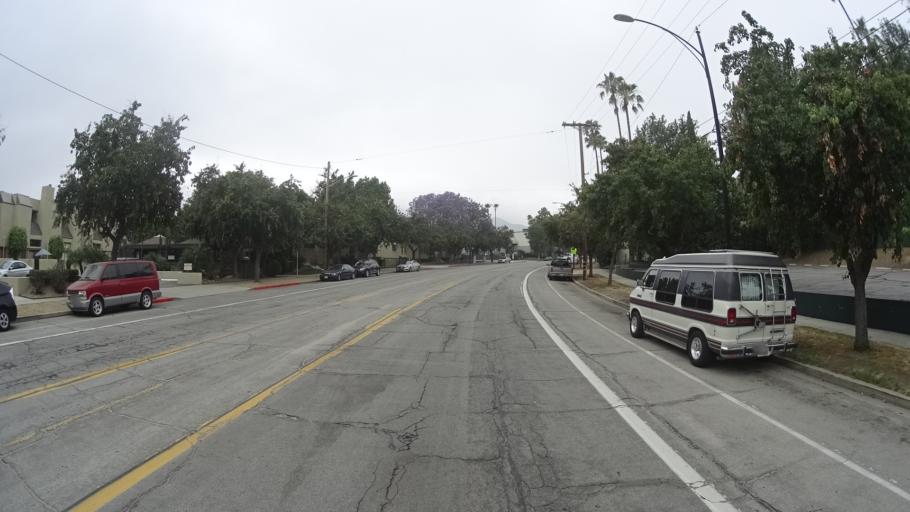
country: US
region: California
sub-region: Los Angeles County
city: Burbank
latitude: 34.1601
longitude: -118.3114
